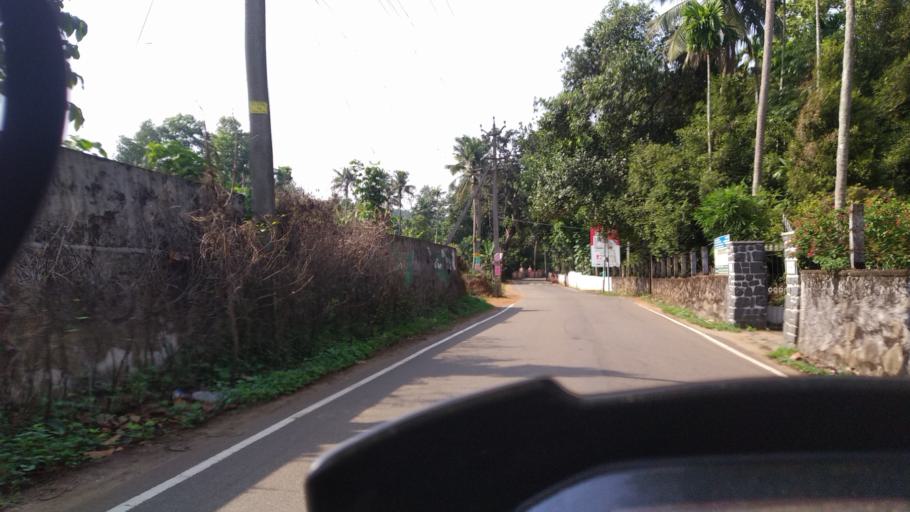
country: IN
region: Kerala
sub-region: Ernakulam
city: Piravam
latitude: 9.8461
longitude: 76.5346
